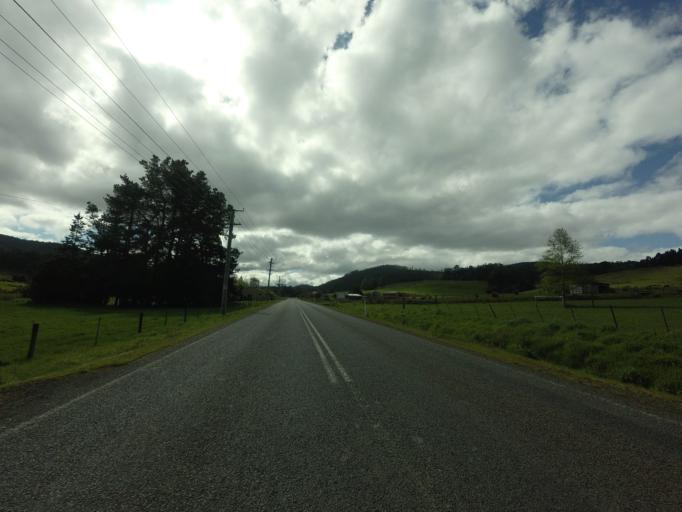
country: AU
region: Tasmania
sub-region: Huon Valley
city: Cygnet
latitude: -43.2946
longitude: 147.0114
